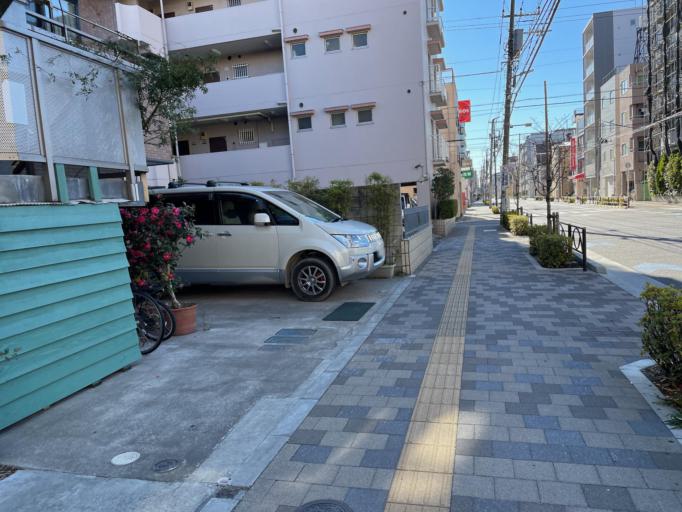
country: JP
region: Tokyo
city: Urayasu
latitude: 35.7032
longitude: 139.8024
